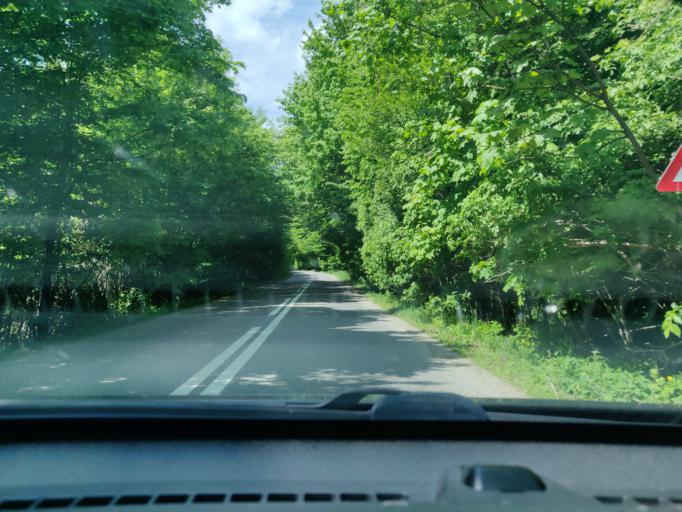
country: RO
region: Vrancea
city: Dragosloveni
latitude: 46.0382
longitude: 26.7059
